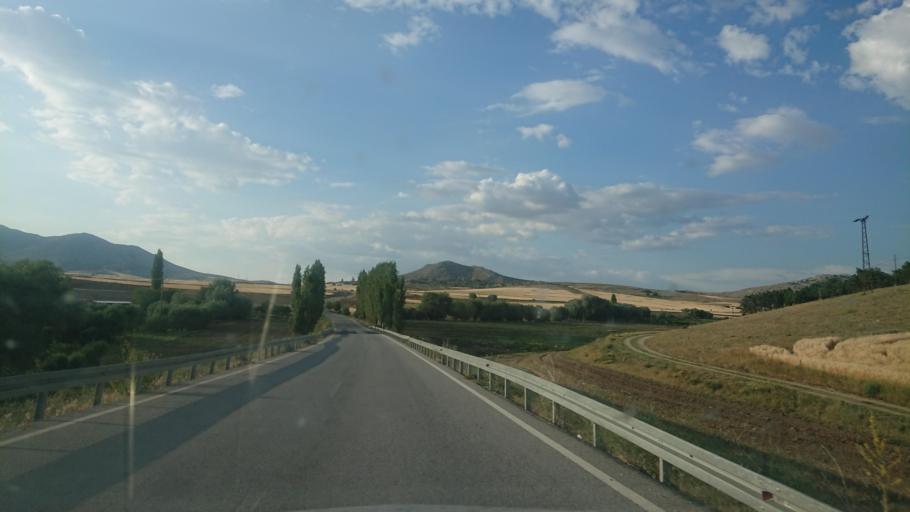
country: TR
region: Aksaray
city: Balci
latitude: 38.5709
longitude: 34.1058
